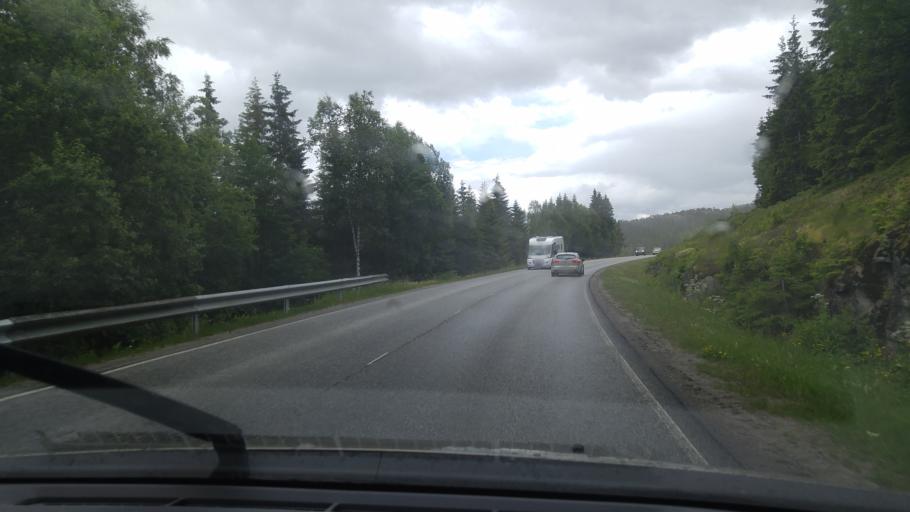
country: NO
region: Nord-Trondelag
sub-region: Namsos
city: Namsos
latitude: 64.4001
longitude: 11.4115
